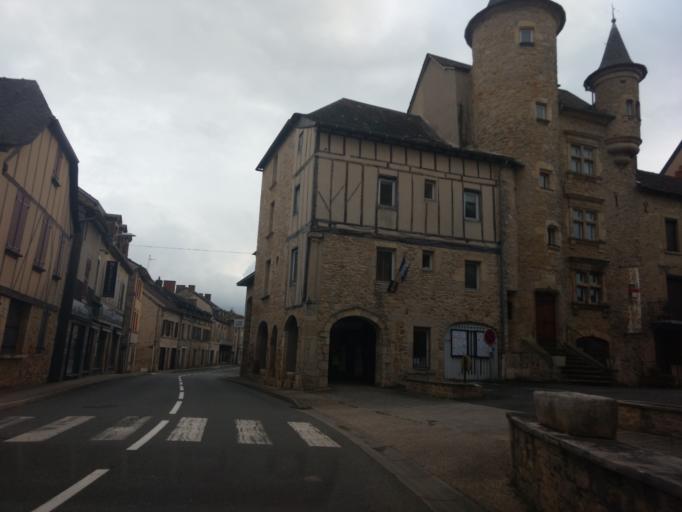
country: FR
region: Midi-Pyrenees
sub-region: Departement de l'Aveyron
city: Montbazens
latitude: 44.4773
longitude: 2.2295
